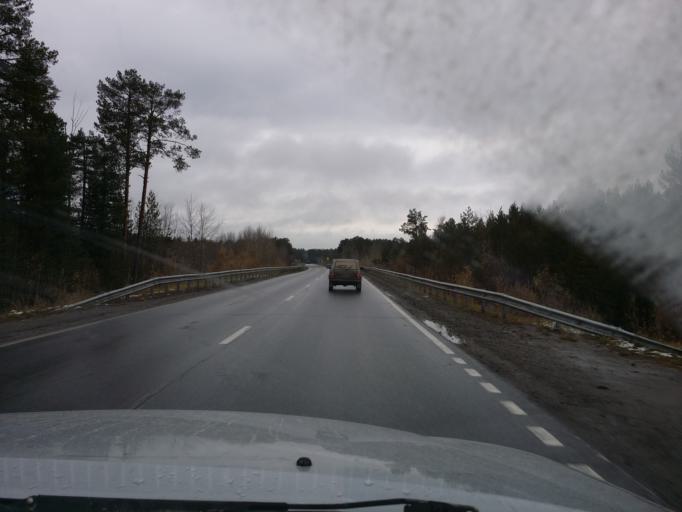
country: RU
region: Khanty-Mansiyskiy Avtonomnyy Okrug
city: Megion
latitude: 61.1169
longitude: 75.8394
